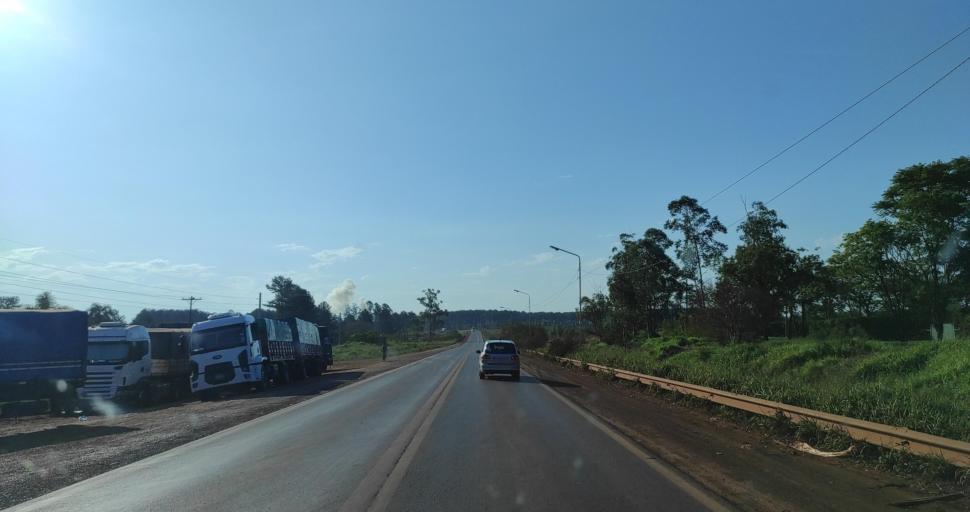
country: AR
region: Corrientes
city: Gobernador Ingeniero Valentin Virasoro
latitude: -28.0258
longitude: -56.0148
